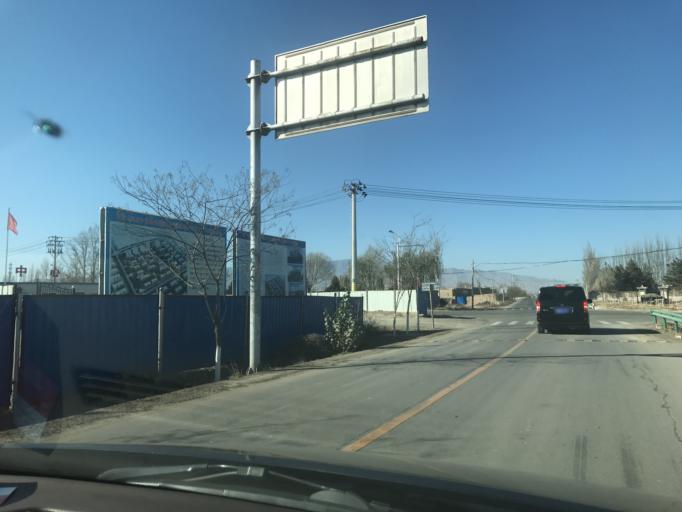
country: CN
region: Gansu Sheng
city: Gulang
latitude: 37.6774
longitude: 102.8358
